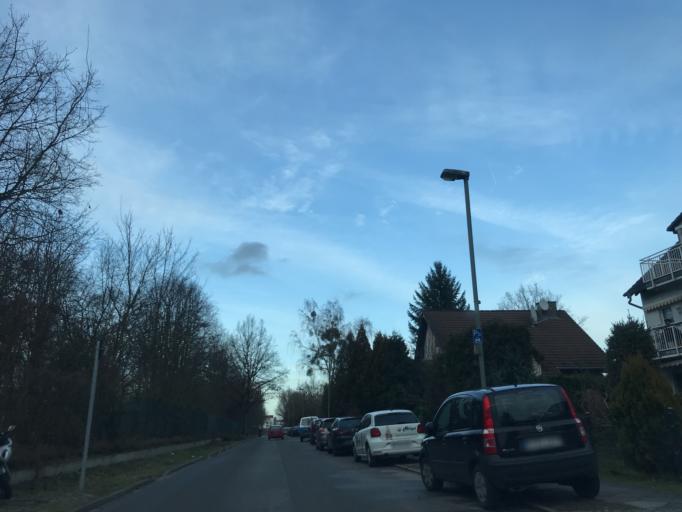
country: DE
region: Berlin
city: Staaken
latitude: 52.5524
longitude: 13.1329
